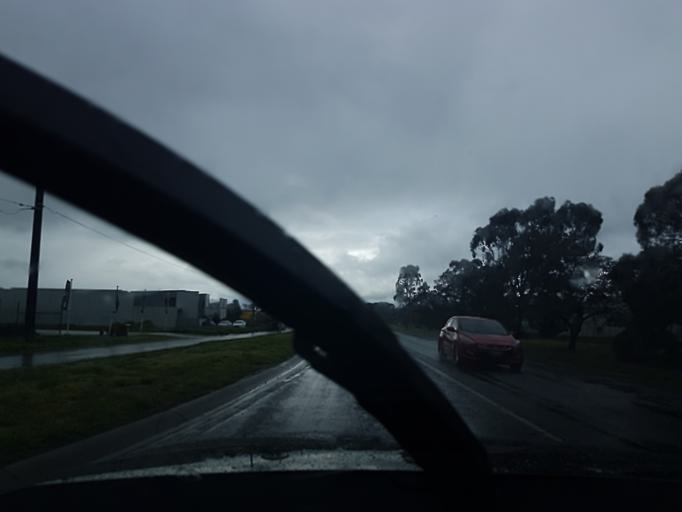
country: AU
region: Victoria
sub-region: Ballarat North
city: Newington
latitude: -37.5443
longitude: 143.7981
